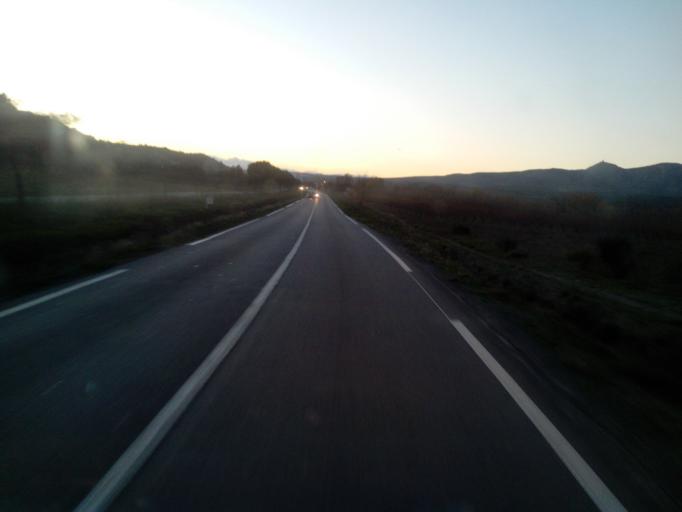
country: FR
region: Languedoc-Roussillon
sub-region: Departement des Pyrenees-Orientales
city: Baixas
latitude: 42.7782
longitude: 2.8237
